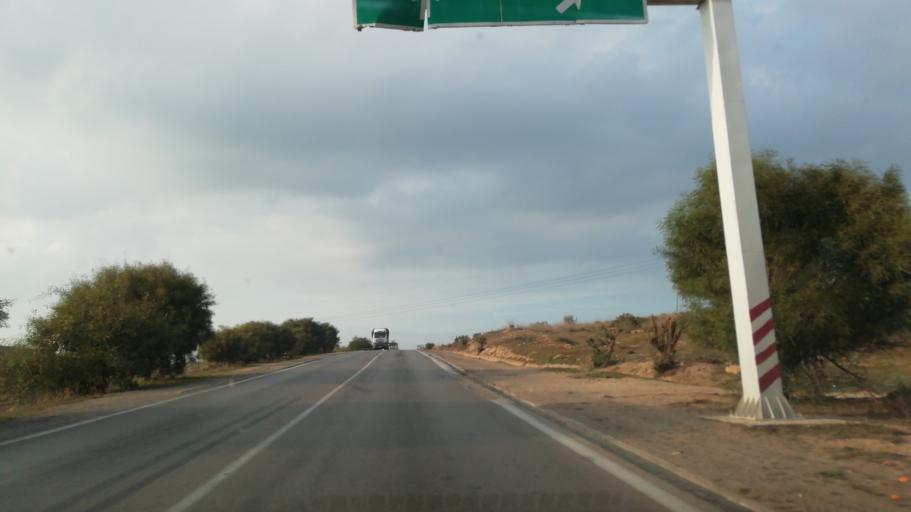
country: DZ
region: Oran
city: Ain el Bya
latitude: 35.7830
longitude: -0.0999
